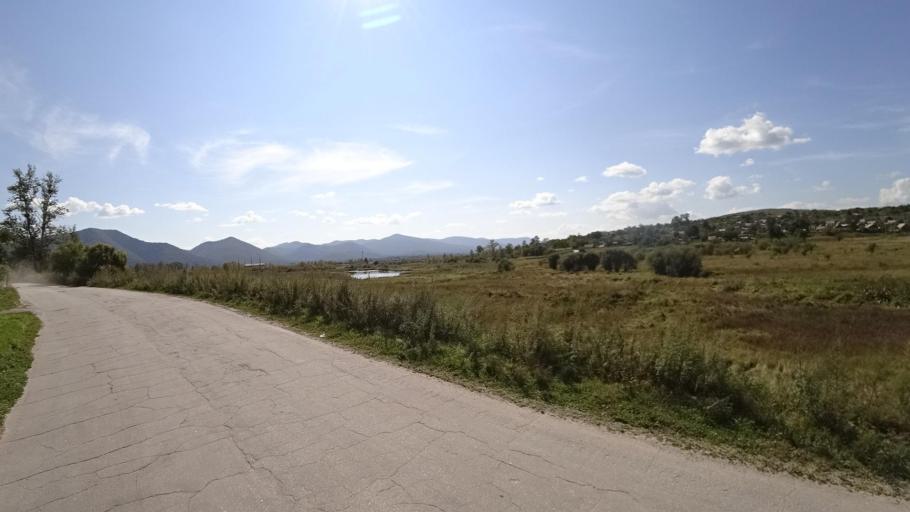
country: RU
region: Jewish Autonomous Oblast
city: Londoko
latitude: 49.0088
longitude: 131.8784
